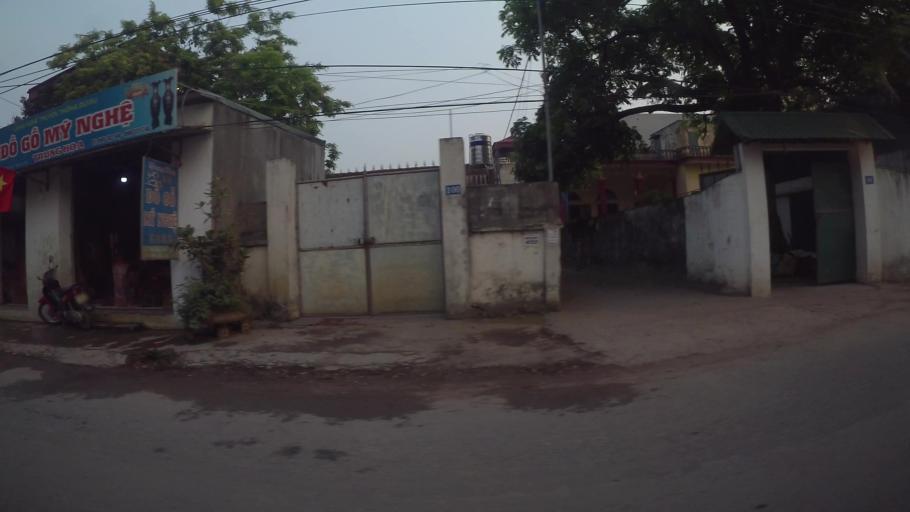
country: VN
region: Ha Noi
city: Thuong Tin
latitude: 20.8701
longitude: 105.8177
